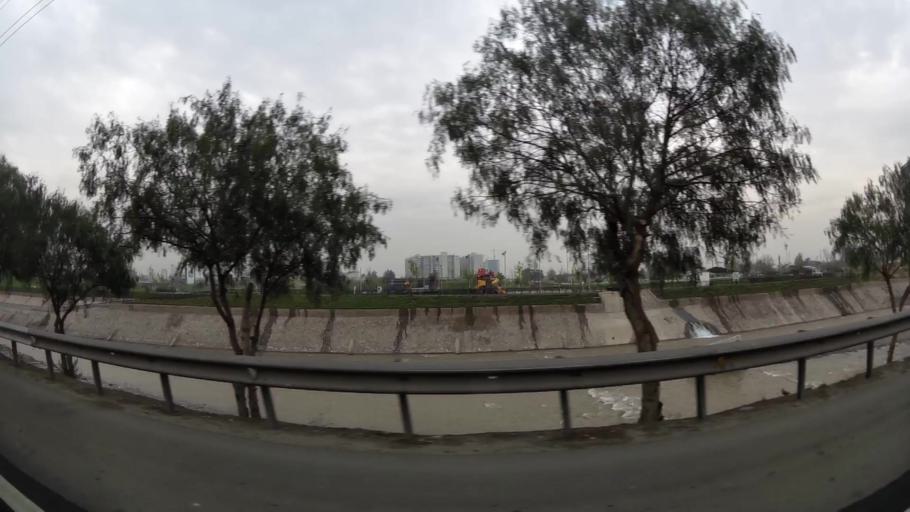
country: CL
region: Santiago Metropolitan
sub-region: Provincia de Santiago
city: Santiago
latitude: -33.4219
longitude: -70.6820
